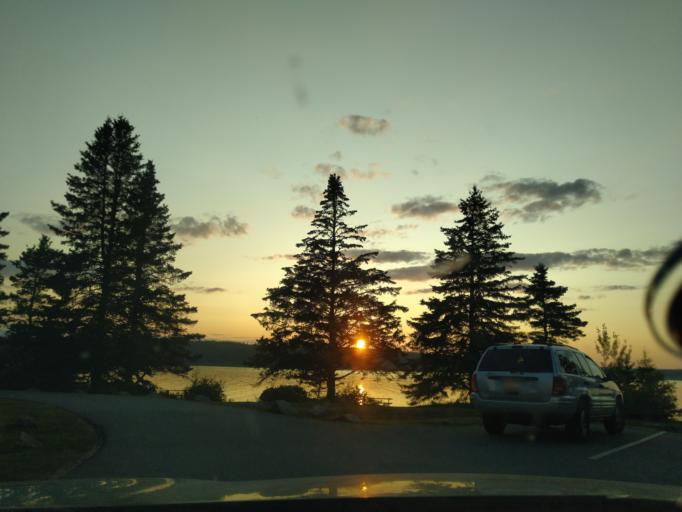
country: US
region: Maine
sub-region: Hancock County
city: Gouldsboro
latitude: 44.3755
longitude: -68.0752
